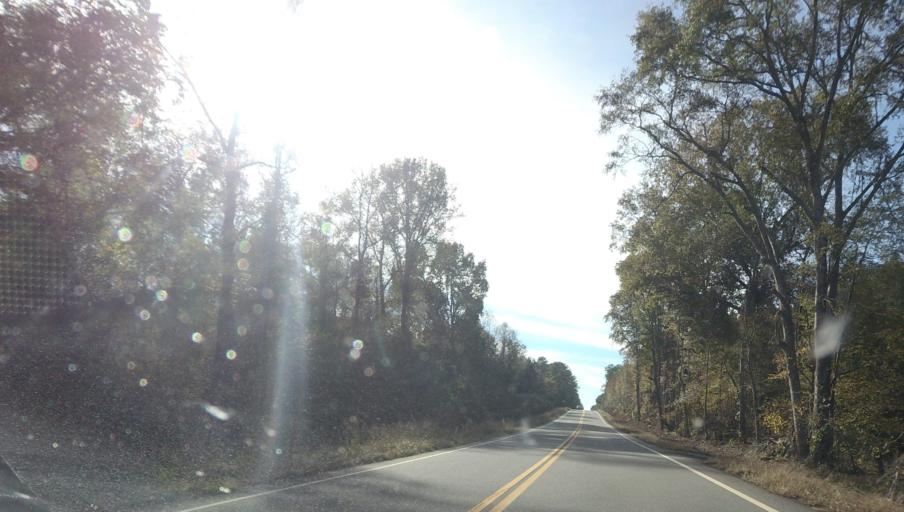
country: US
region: Georgia
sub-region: Taylor County
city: Butler
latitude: 32.7183
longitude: -84.2533
